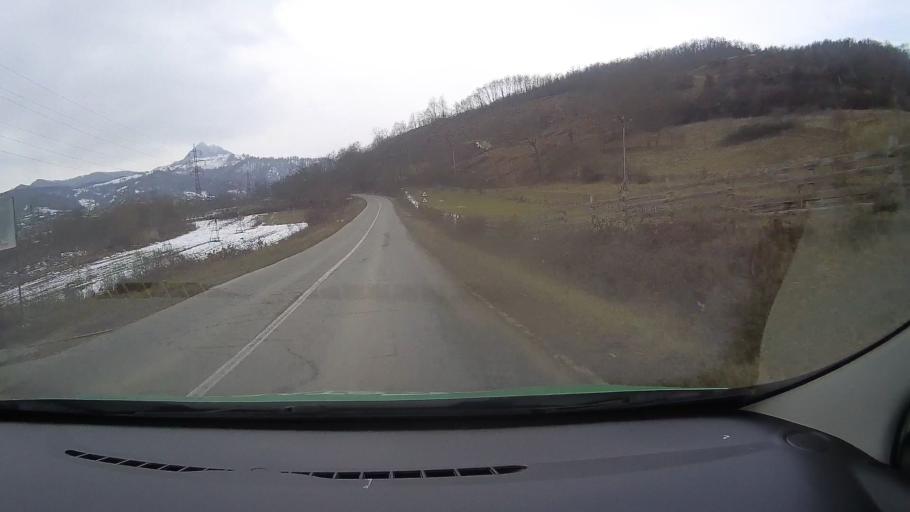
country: RO
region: Alba
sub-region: Oras Zlatna
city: Fenes
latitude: 46.0908
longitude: 23.2795
